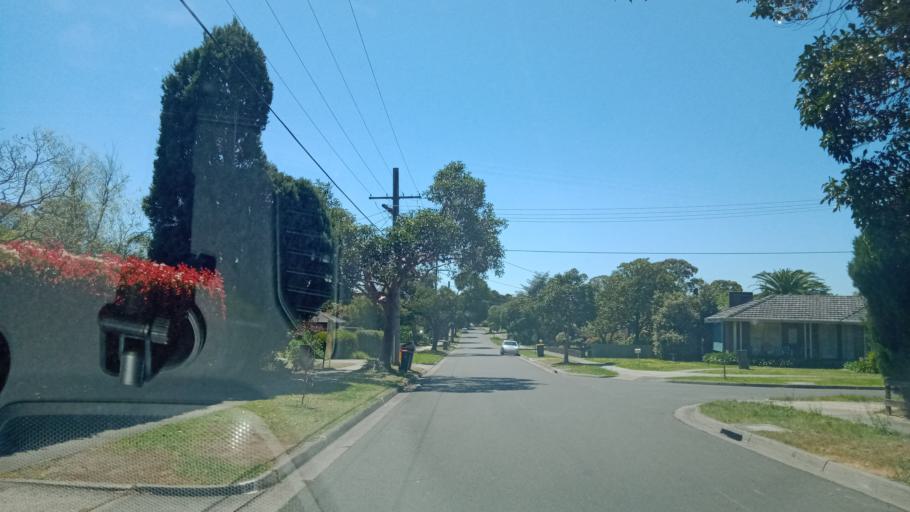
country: AU
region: Victoria
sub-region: Greater Dandenong
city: Springvale
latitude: -37.9241
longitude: 145.1629
